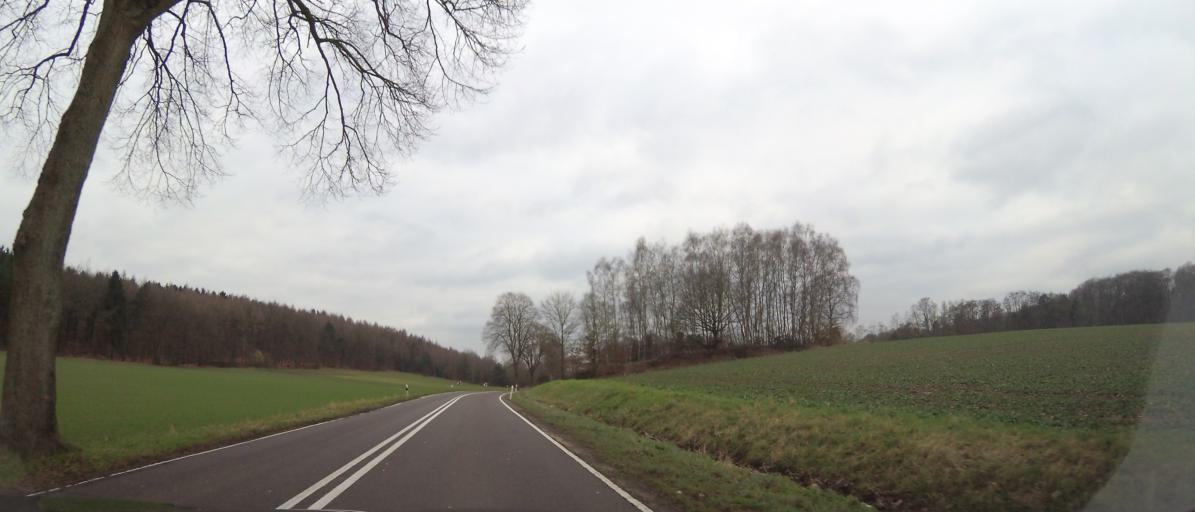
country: DE
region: Saarland
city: Puttlingen
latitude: 49.3160
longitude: 6.8656
